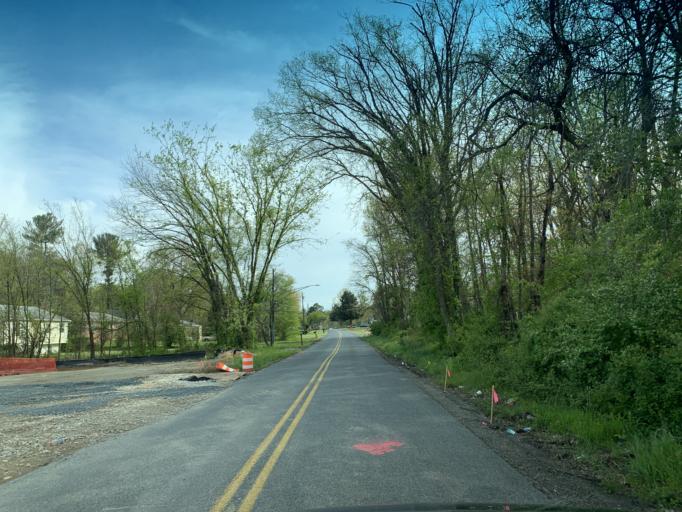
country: US
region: Maryland
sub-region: Harford County
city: Perryman
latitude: 39.4846
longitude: -76.2059
